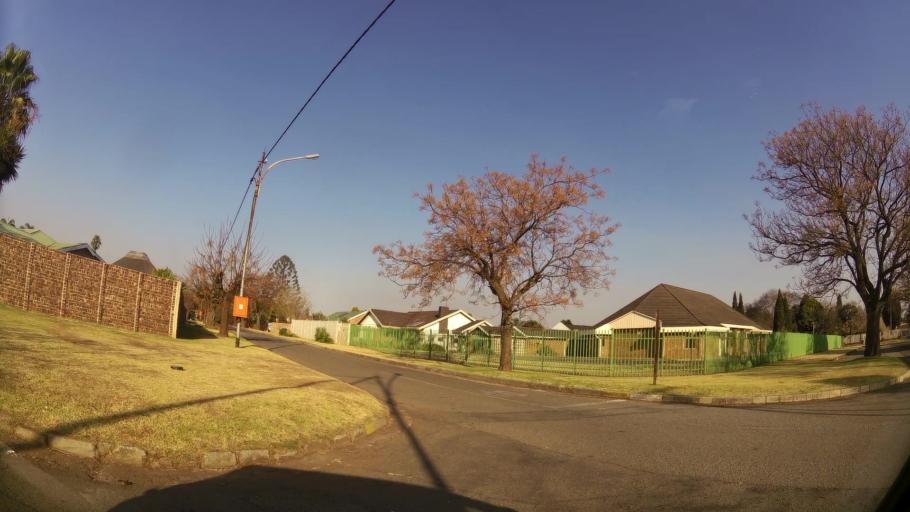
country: ZA
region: Gauteng
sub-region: Ekurhuleni Metropolitan Municipality
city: Springs
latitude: -26.2603
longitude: 28.3903
